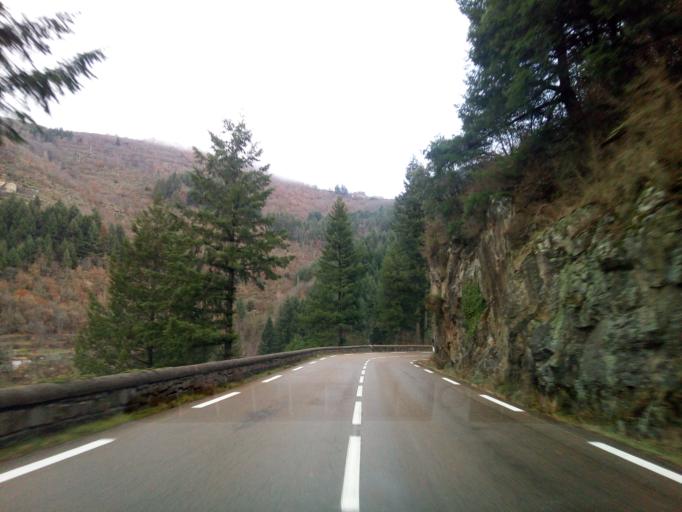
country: FR
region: Rhone-Alpes
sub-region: Departement de l'Ardeche
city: Le Cheylard
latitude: 44.8896
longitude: 4.5058
